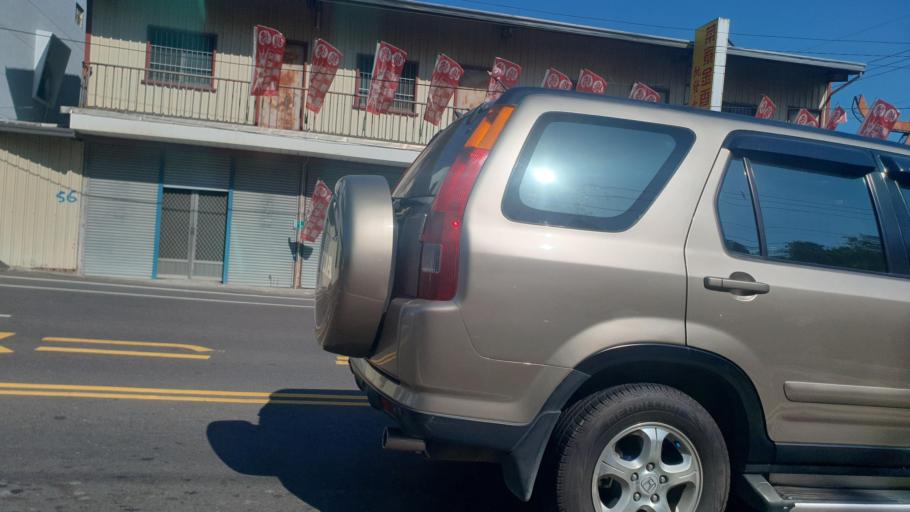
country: TW
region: Taiwan
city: Yujing
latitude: 23.0640
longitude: 120.3874
